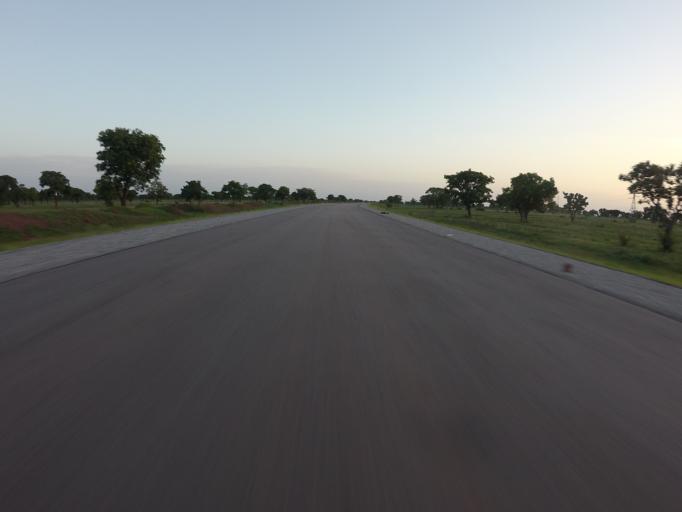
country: GH
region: Northern
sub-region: Yendi
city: Yendi
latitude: 9.9548
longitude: -0.1522
